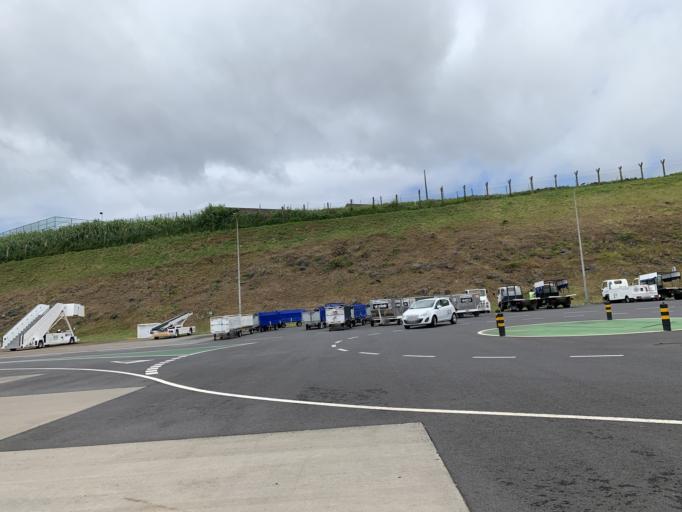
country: PT
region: Azores
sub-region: Ponta Delgada
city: Arrifes
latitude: 37.7493
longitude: -25.7121
